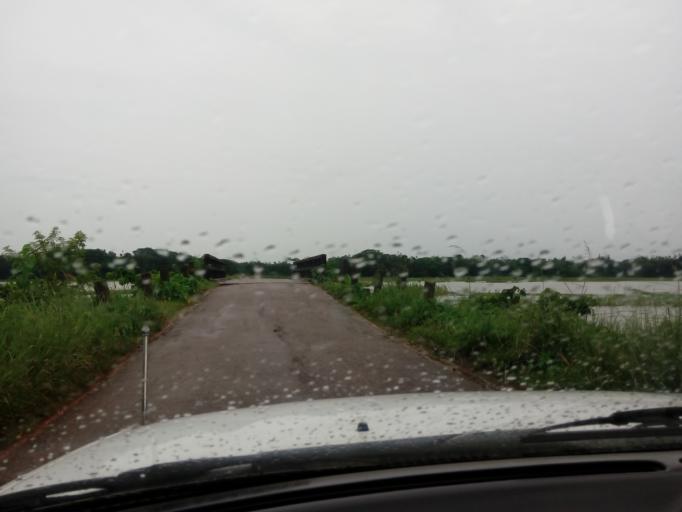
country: BD
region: Sylhet
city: Sylhet
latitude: 24.9618
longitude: 91.7959
